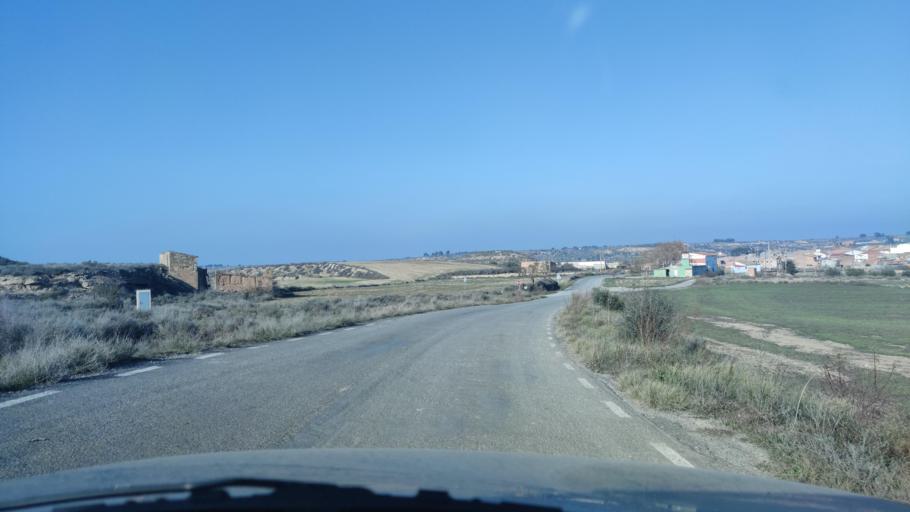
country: ES
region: Catalonia
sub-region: Provincia de Lleida
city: Torrebesses
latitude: 41.4539
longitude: 0.5577
